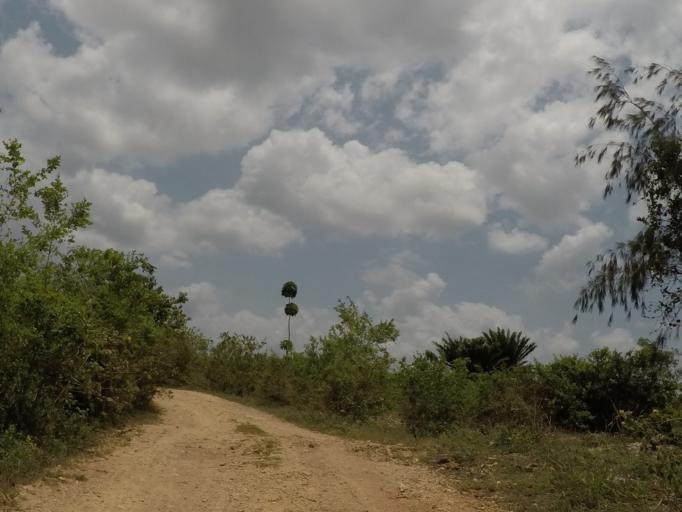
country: TZ
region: Zanzibar Central/South
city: Koani
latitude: -6.1759
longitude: 39.3115
